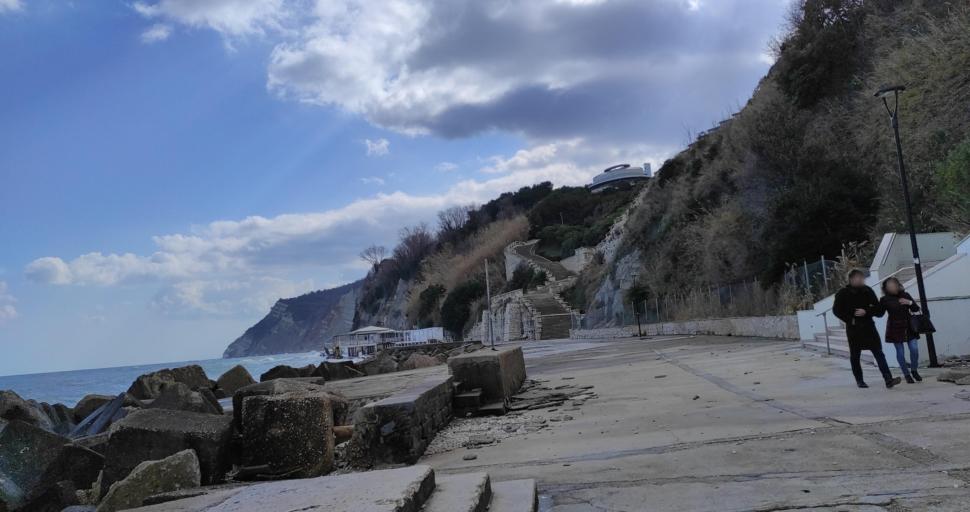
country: IT
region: The Marches
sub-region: Provincia di Ancona
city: Pietra la Croce
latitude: 43.6164
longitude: 13.5340
